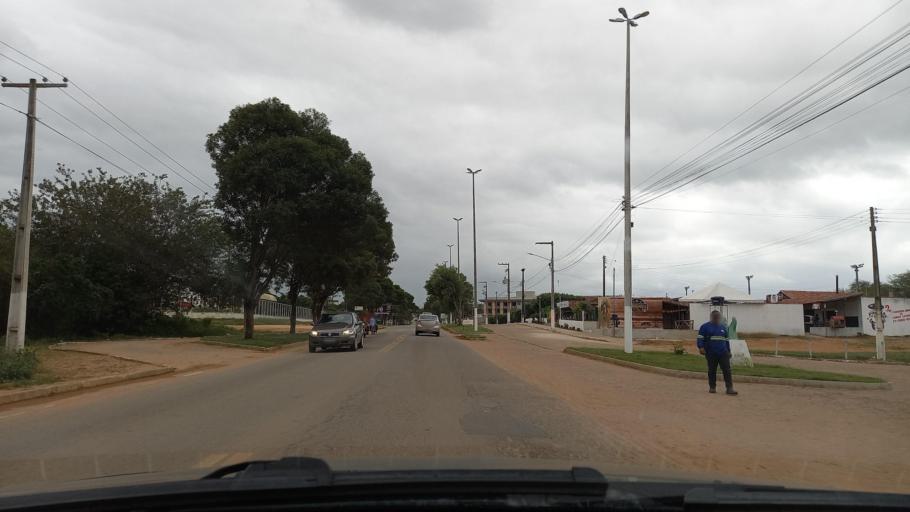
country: BR
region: Sergipe
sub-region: Caninde De Sao Francisco
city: Caninde de Sao Francisco
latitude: -9.6707
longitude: -37.7935
